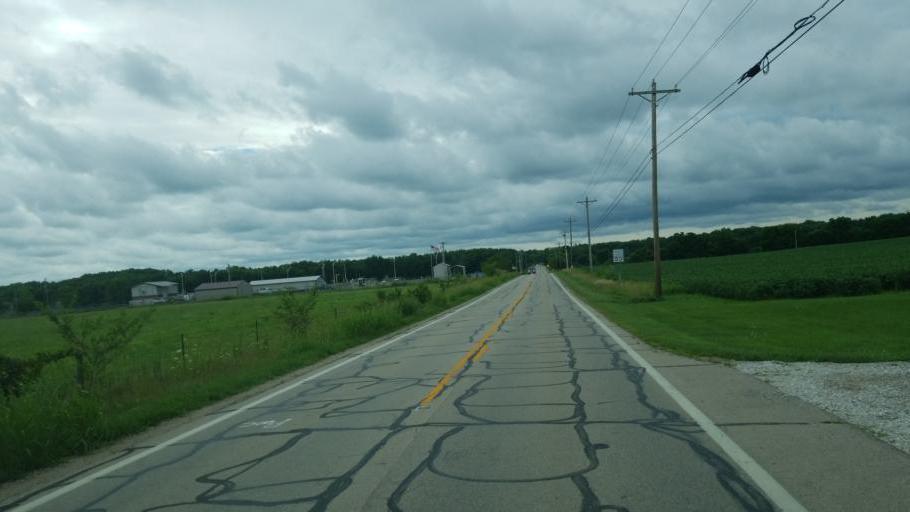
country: US
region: Ohio
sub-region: Pickaway County
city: South Bloomfield
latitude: 39.7193
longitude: -83.0036
